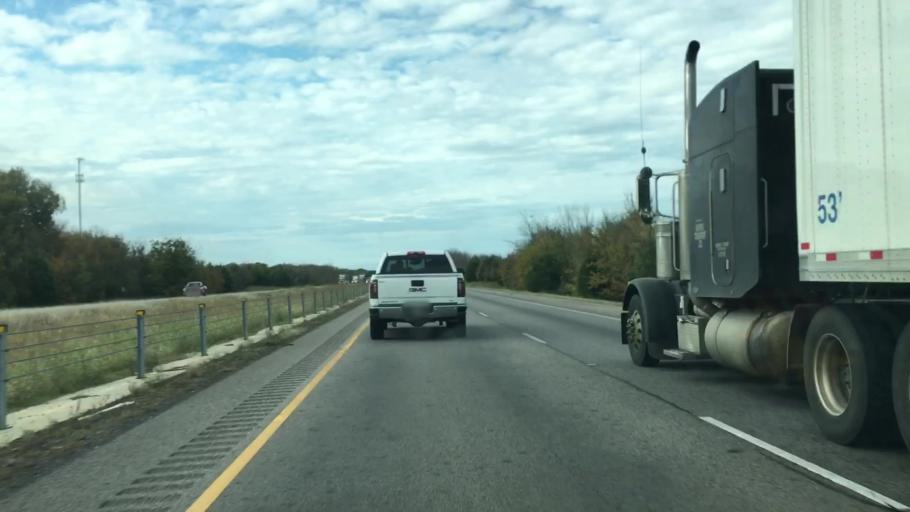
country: US
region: Arkansas
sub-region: Conway County
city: Morrilton
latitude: 35.2029
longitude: -92.8087
